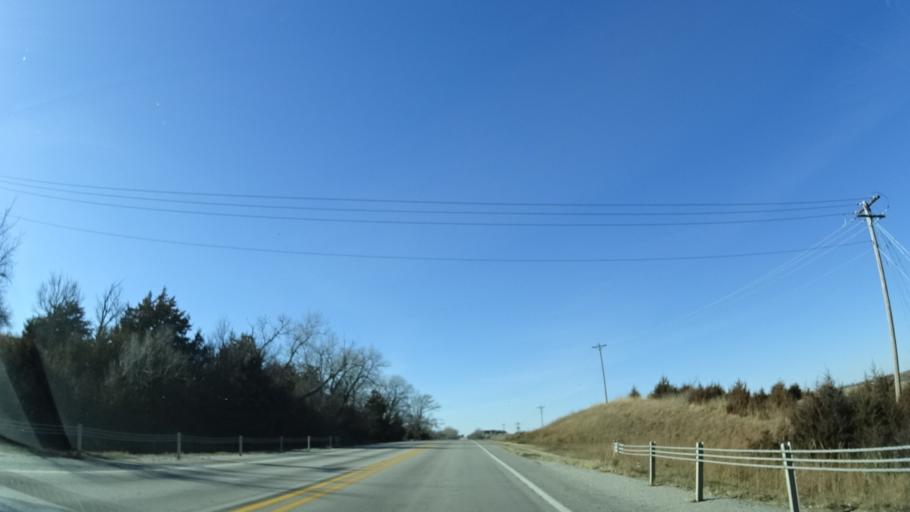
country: US
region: Nebraska
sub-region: Cass County
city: Louisville
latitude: 40.9796
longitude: -96.1826
